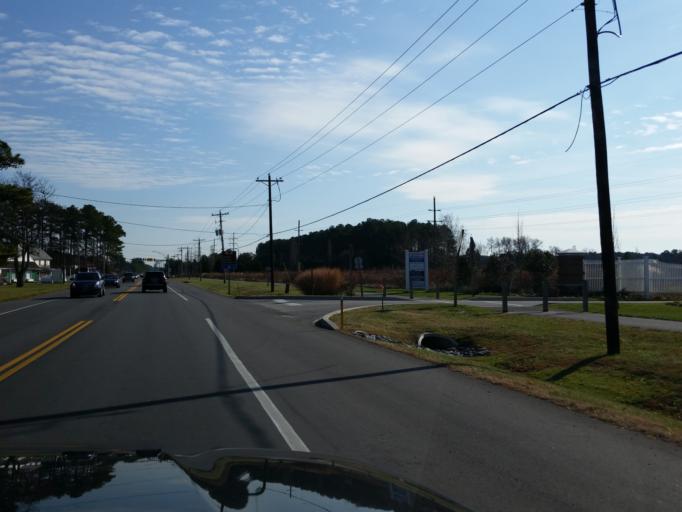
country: US
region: Maryland
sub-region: Talbot County
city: Saint Michaels
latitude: 38.7767
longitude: -76.2168
